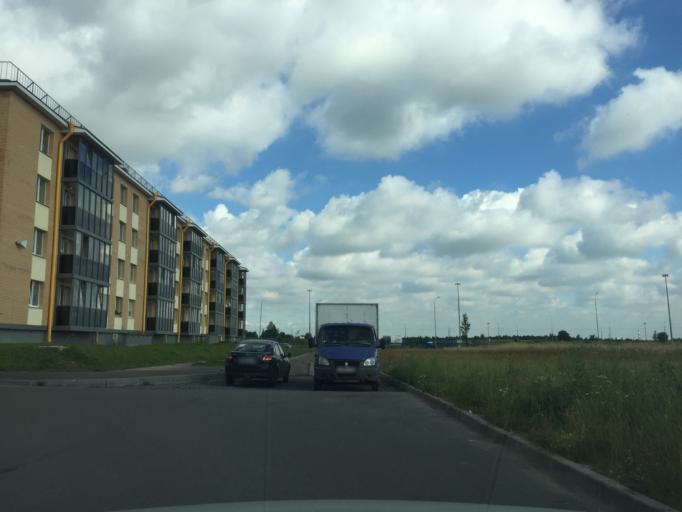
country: RU
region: St.-Petersburg
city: Pushkin
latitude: 59.7538
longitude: 30.3760
